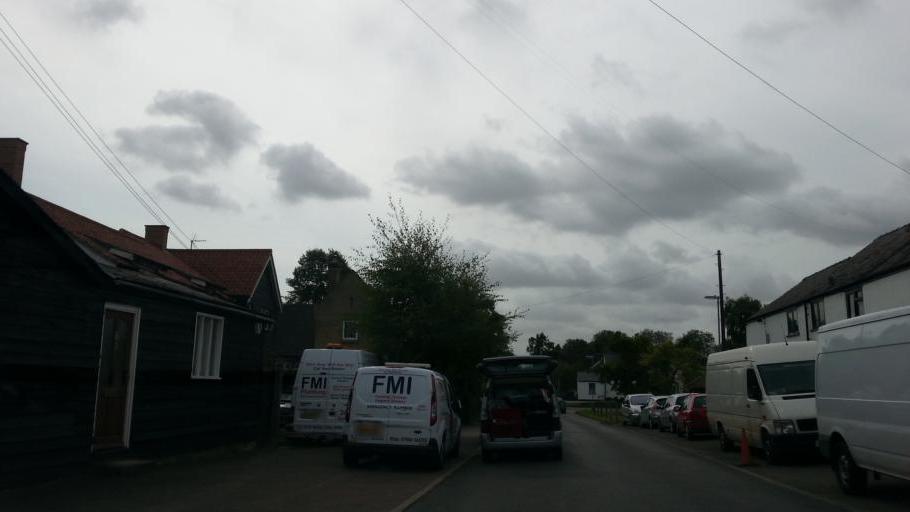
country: GB
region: England
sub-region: Cambridgeshire
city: Comberton
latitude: 52.1878
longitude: 0.0188
